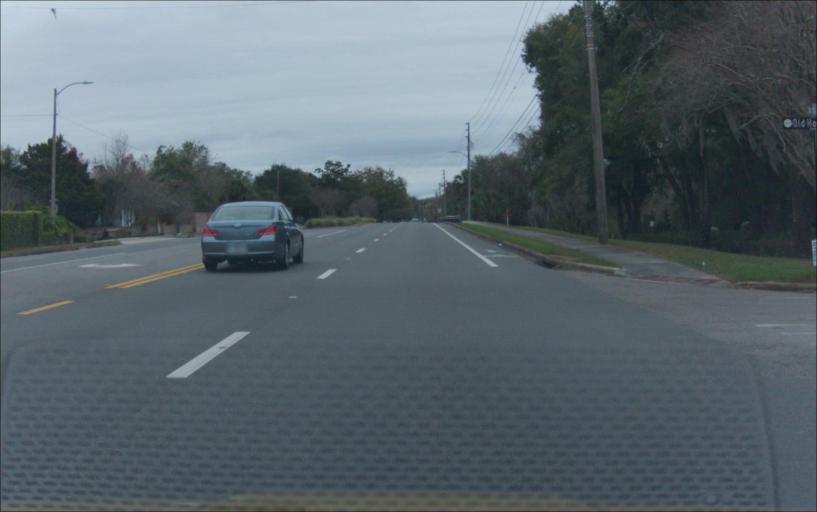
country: US
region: Florida
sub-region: Orange County
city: Maitland
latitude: 28.6253
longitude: -81.3395
